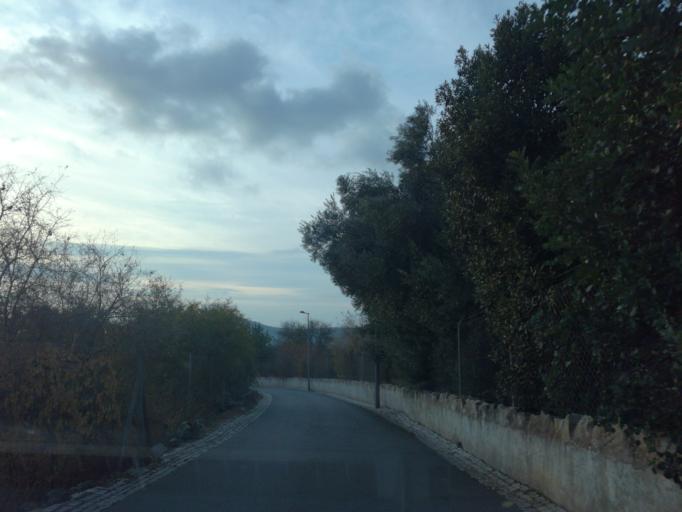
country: PT
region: Faro
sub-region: Sao Bras de Alportel
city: Sao Bras de Alportel
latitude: 37.0977
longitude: -7.8975
